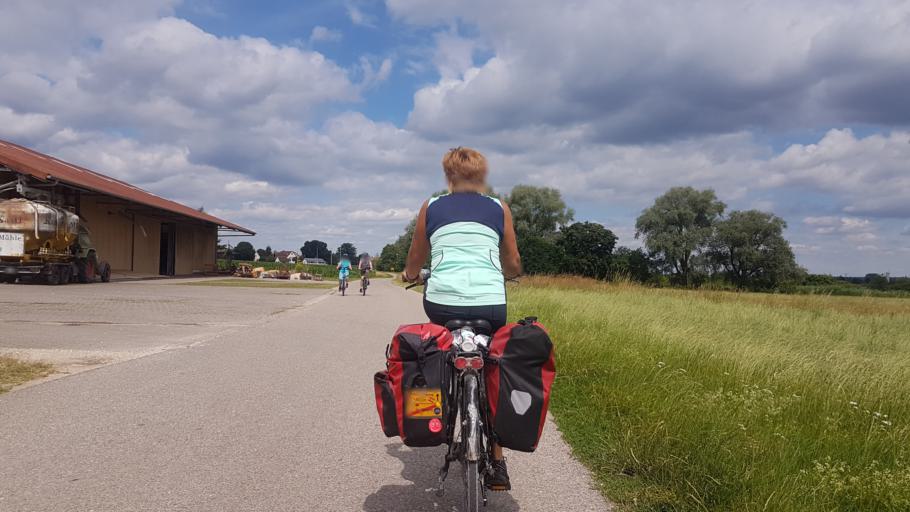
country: DE
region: Bavaria
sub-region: Regierungsbezirk Mittelfranken
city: Gunzenhausen
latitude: 49.0914
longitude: 10.7607
